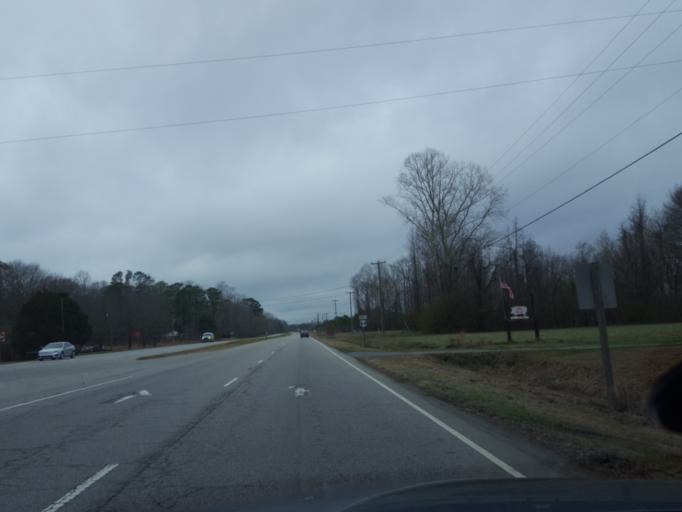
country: US
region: North Carolina
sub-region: Washington County
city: Plymouth
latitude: 35.8102
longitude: -76.8693
